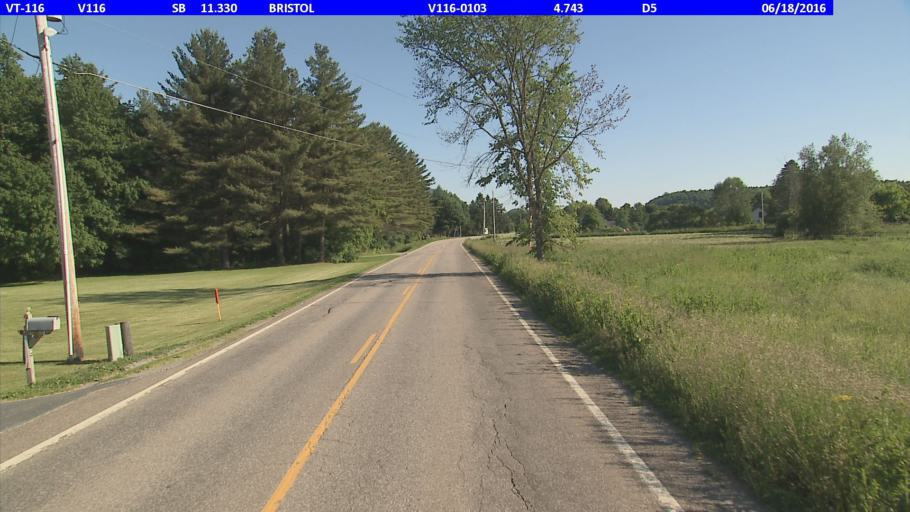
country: US
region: Vermont
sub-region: Addison County
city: Bristol
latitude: 44.1189
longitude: -73.0962
